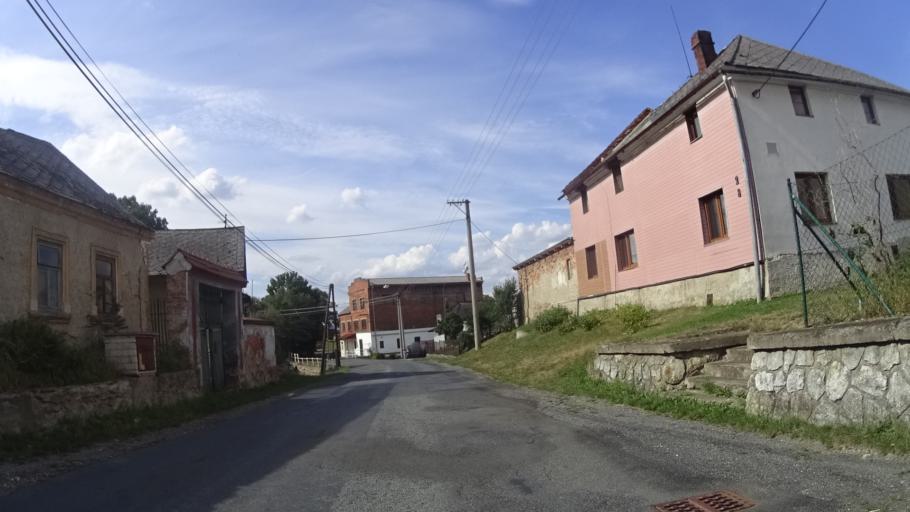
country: CZ
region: Olomoucky
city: Moravicany
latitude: 49.7473
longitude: 16.9748
